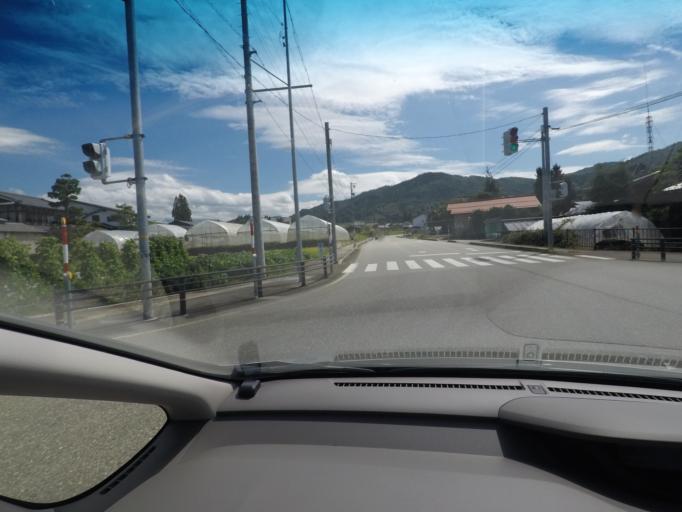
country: JP
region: Gifu
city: Takayama
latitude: 36.1362
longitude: 137.2907
